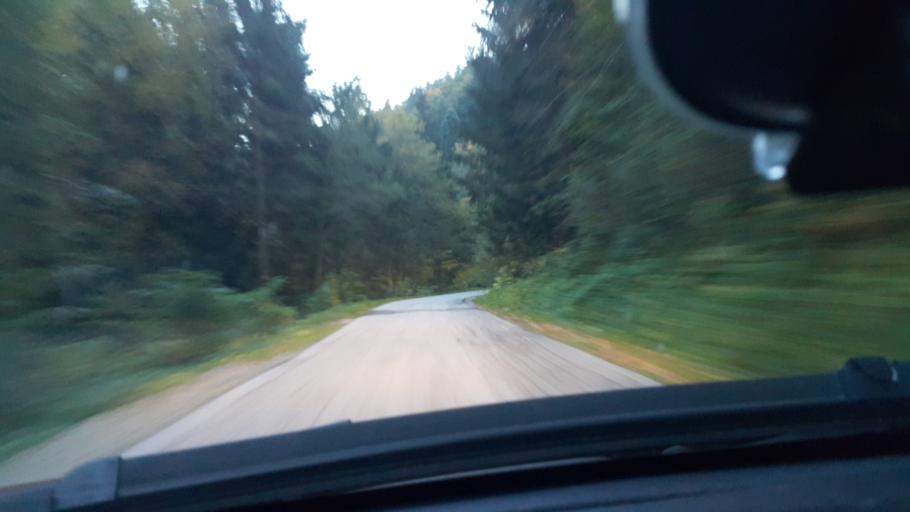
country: SI
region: Vitanje
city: Vitanje
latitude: 46.4052
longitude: 15.2948
